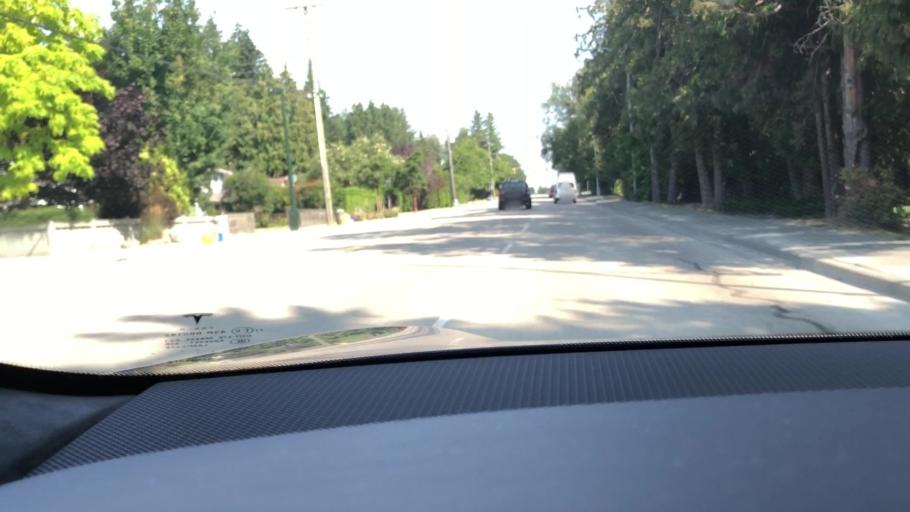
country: US
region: Washington
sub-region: Whatcom County
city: Point Roberts
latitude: 49.0160
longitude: -123.0686
